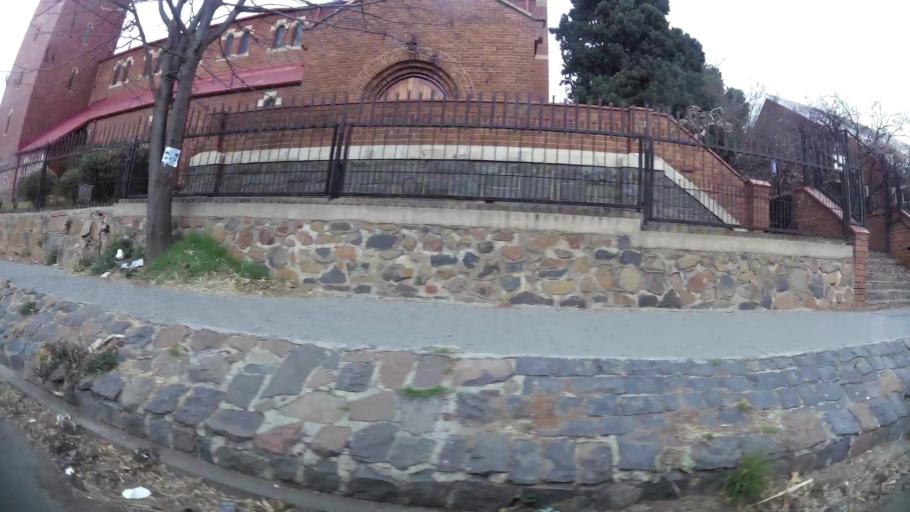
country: ZA
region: Orange Free State
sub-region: Mangaung Metropolitan Municipality
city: Bloemfontein
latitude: -29.1209
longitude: 26.2191
